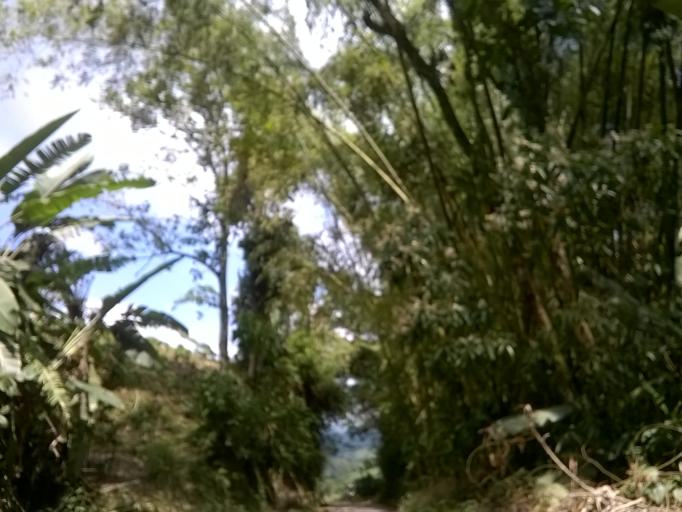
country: CO
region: Quindio
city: Circasia
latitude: 4.5951
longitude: -75.6281
